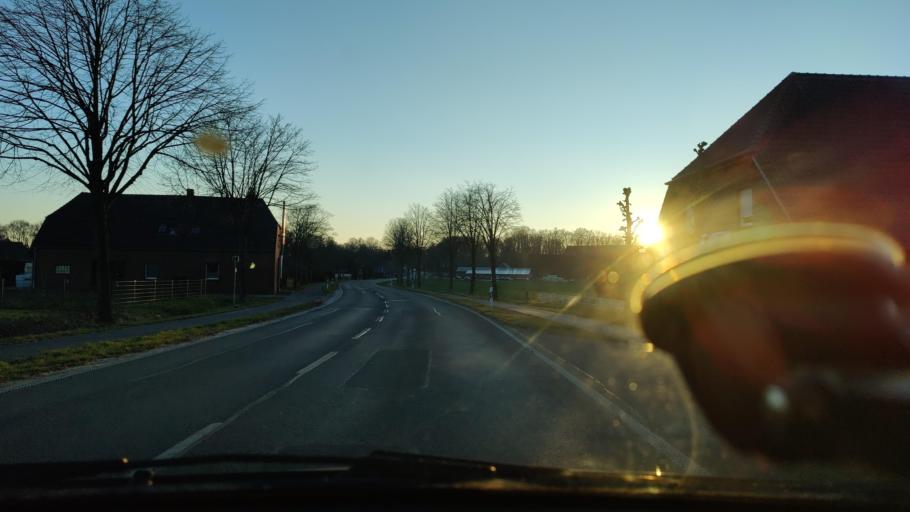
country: DE
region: North Rhine-Westphalia
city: Kalkar
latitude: 51.7339
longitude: 6.2814
